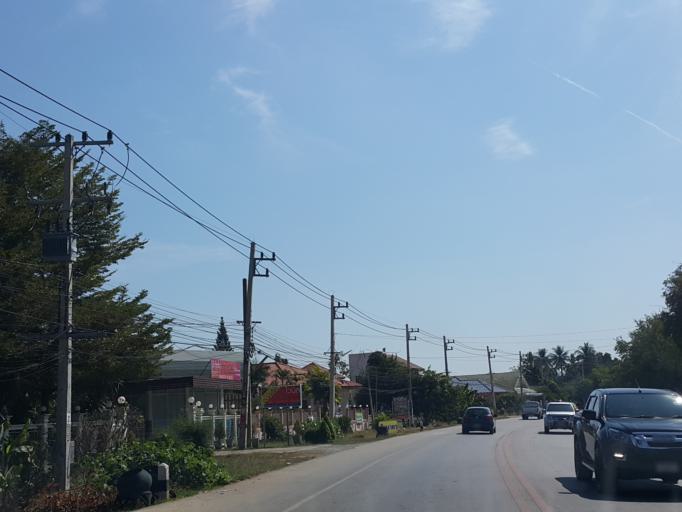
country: TH
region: Sukhothai
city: Sawankhalok
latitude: 17.2883
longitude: 99.8427
